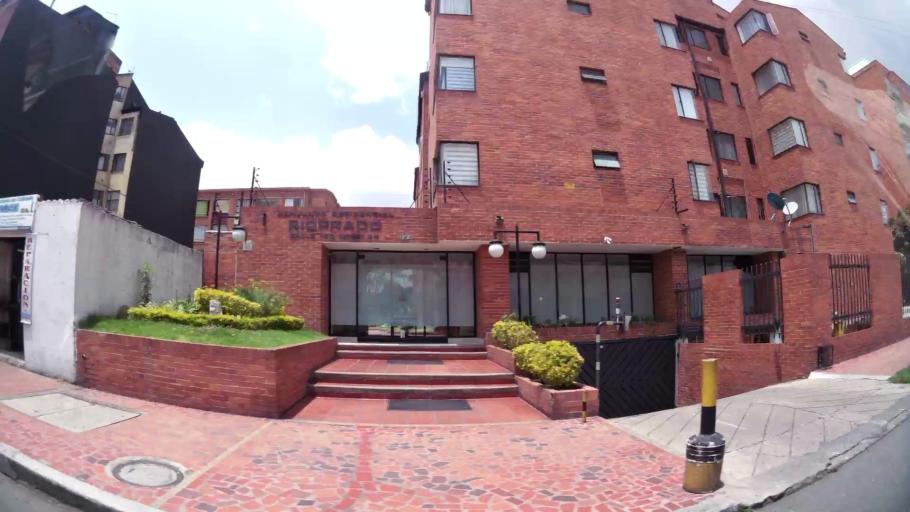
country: CO
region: Bogota D.C.
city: Barrio San Luis
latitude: 4.7390
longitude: -74.0450
